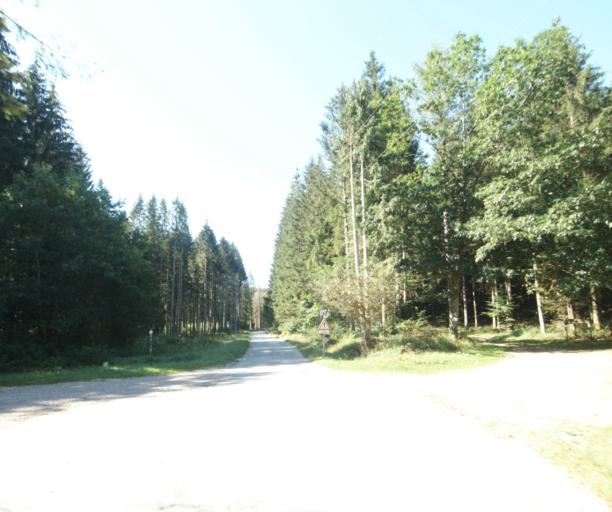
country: FR
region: Lorraine
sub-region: Departement des Vosges
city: Arches
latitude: 48.1545
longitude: 6.5093
